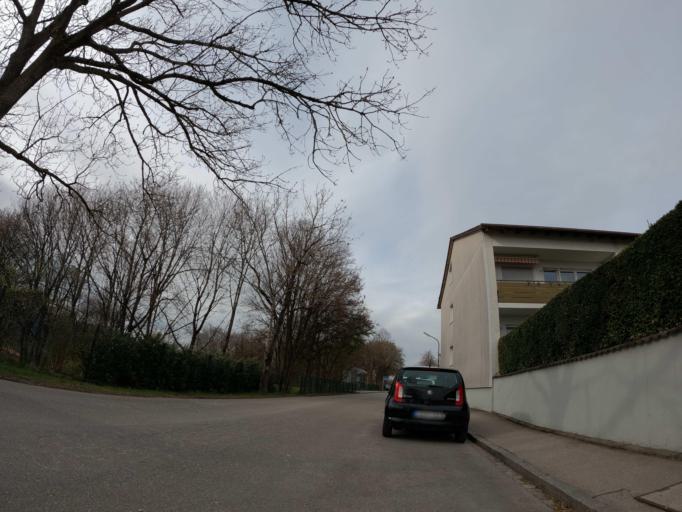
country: DE
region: Bavaria
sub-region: Upper Bavaria
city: Taufkirchen
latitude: 48.0431
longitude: 11.6225
